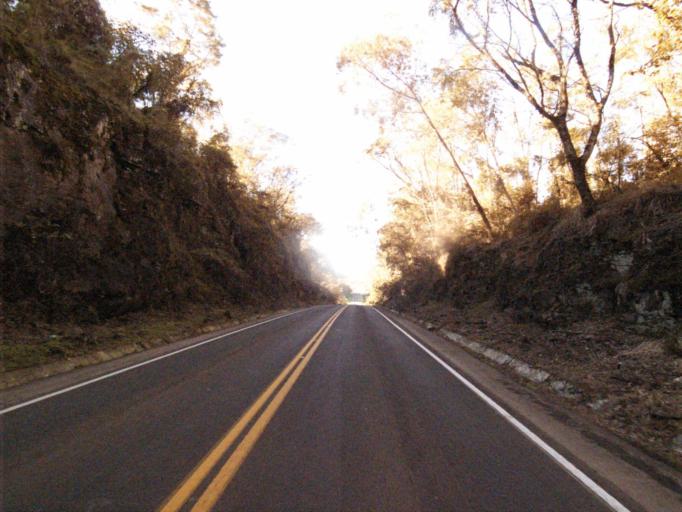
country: AR
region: Misiones
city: Bernardo de Irigoyen
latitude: -26.5055
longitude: -53.5118
